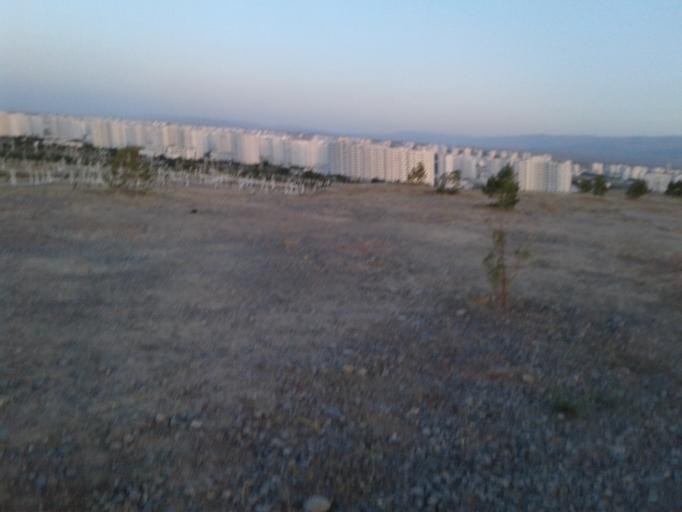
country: TM
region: Ahal
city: Ashgabat
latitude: 37.9250
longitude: 58.3433
